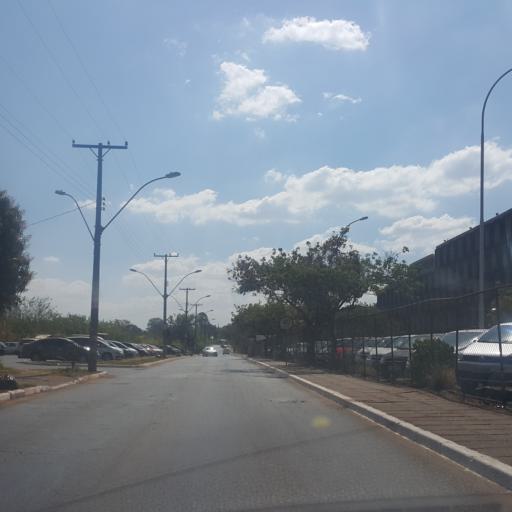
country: BR
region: Federal District
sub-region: Brasilia
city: Brasilia
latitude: -15.8237
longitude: -48.0701
